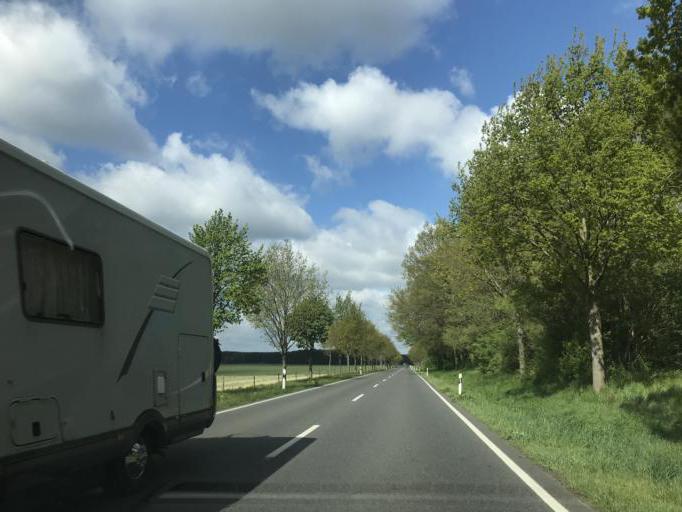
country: DE
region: Brandenburg
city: Marienwerder
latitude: 52.8543
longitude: 13.5644
